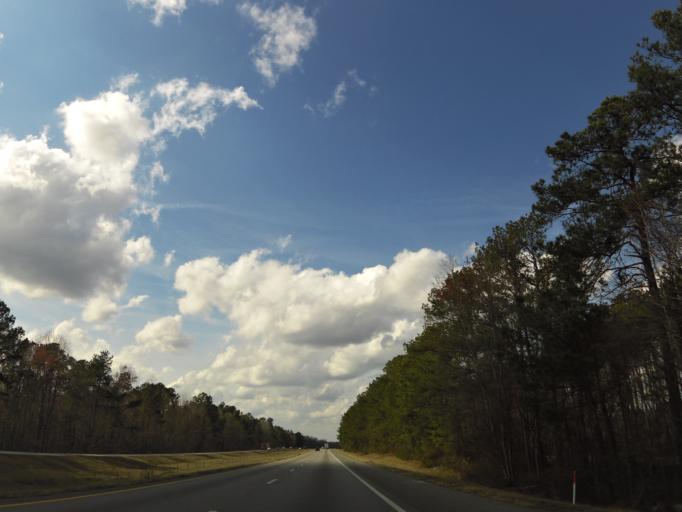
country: US
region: South Carolina
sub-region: Dorchester County
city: Summerville
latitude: 33.0906
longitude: -80.2245
